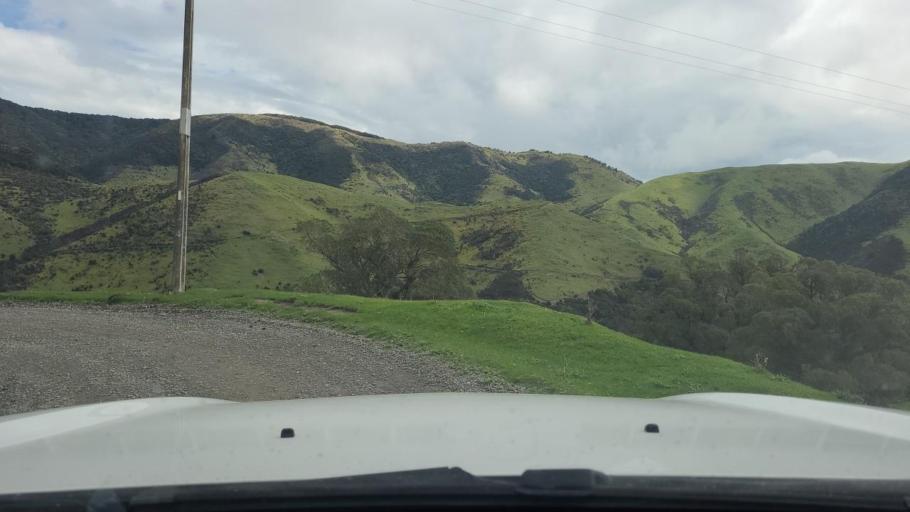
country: NZ
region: Wellington
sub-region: South Wairarapa District
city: Waipawa
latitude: -41.3654
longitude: 175.3864
